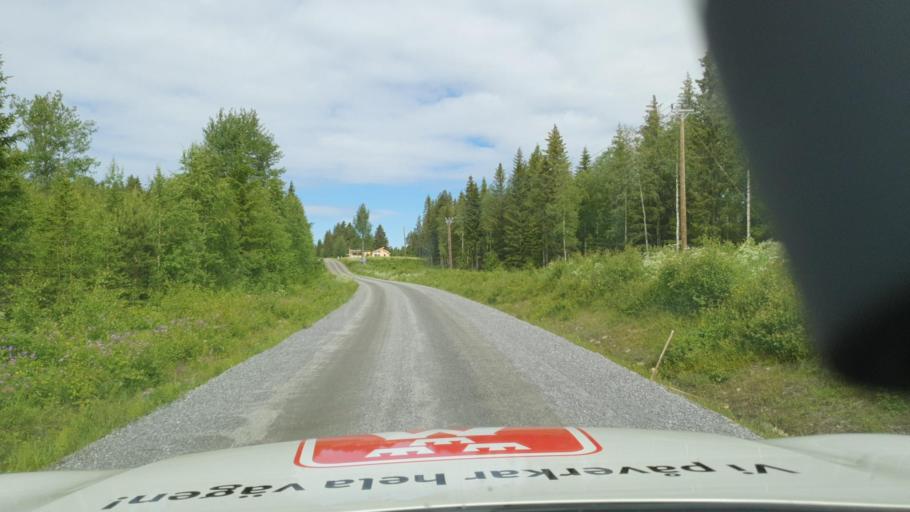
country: SE
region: Vaesterbotten
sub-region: Skelleftea Kommun
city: Langsele
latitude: 64.6175
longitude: 20.2683
